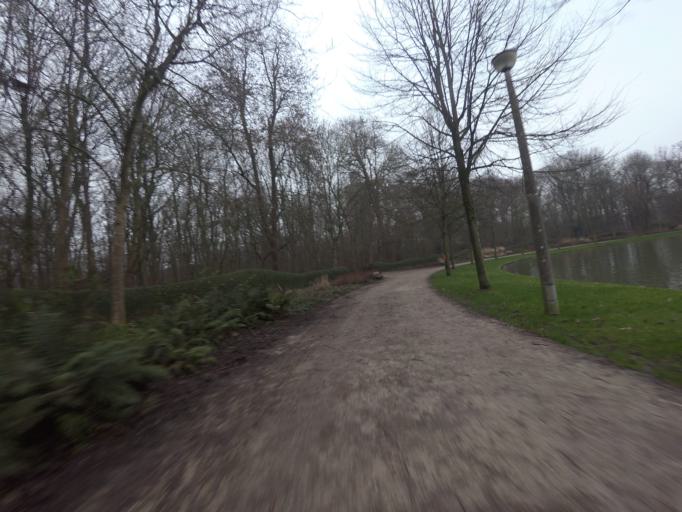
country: BE
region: Flanders
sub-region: Provincie West-Vlaanderen
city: Ostend
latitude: 51.2193
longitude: 2.9260
